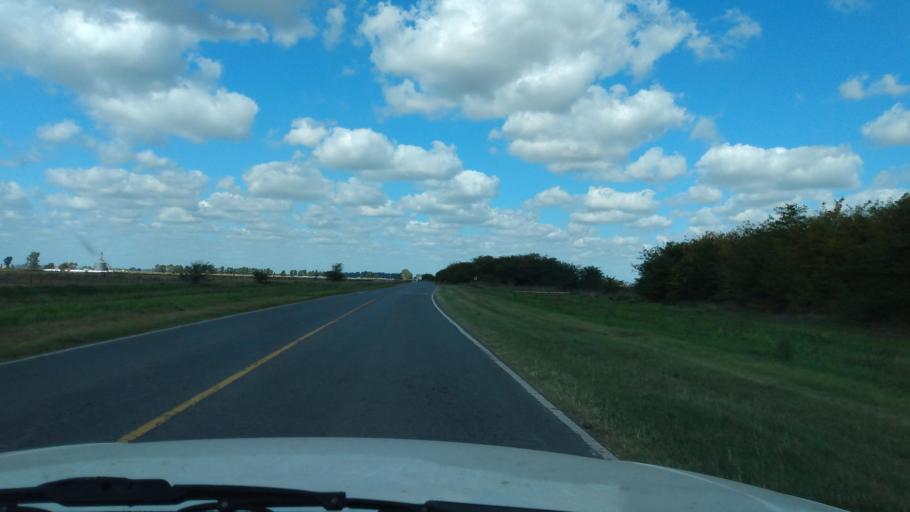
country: AR
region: Buenos Aires
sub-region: Partido de Navarro
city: Navarro
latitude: -34.9610
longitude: -59.3184
